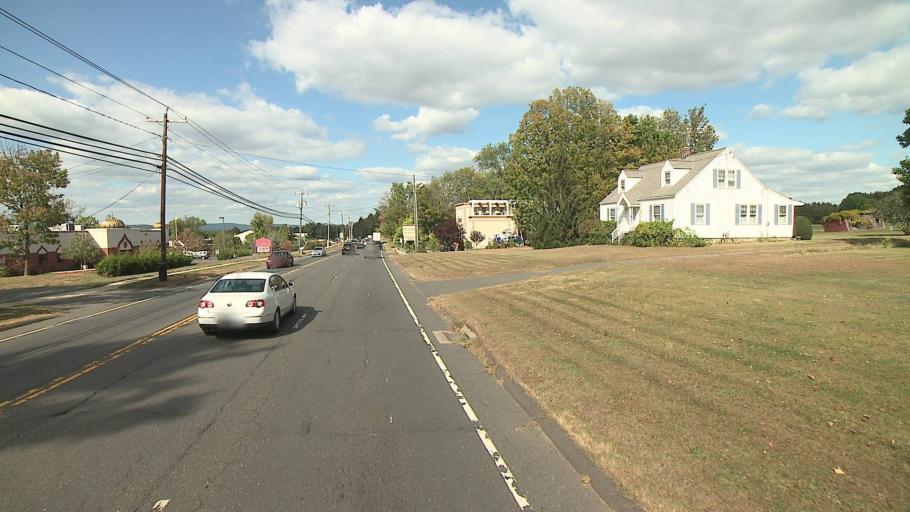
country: US
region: Connecticut
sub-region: Hartford County
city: Plainville
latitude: 41.6315
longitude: -72.9000
